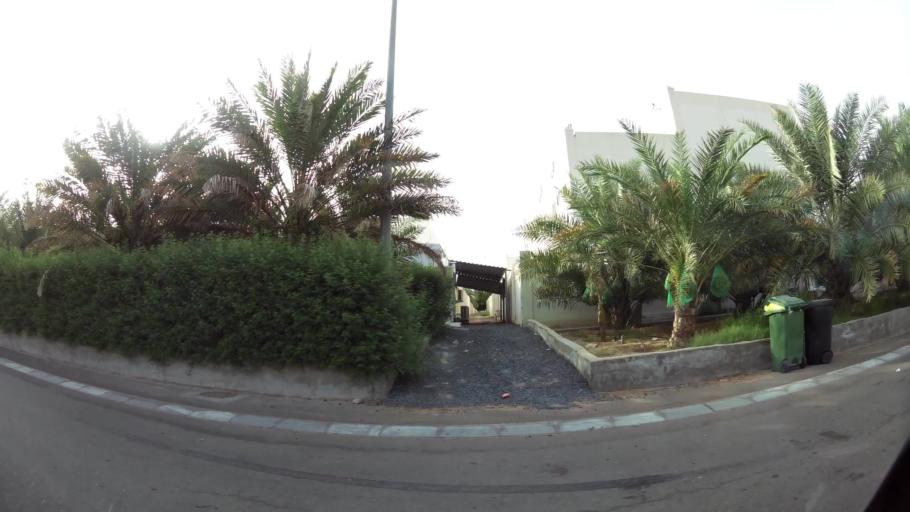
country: AE
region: Abu Dhabi
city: Al Ain
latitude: 24.1112
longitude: 55.7035
